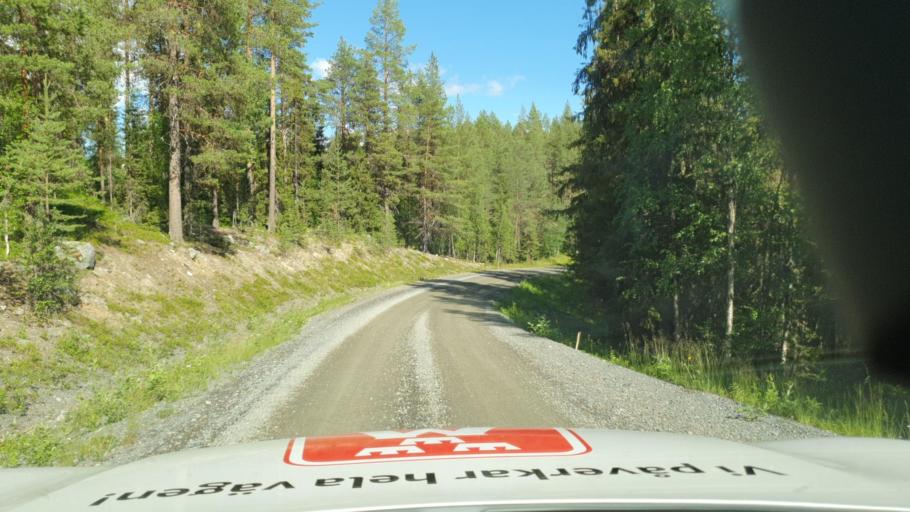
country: SE
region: Vaesterbotten
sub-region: Sorsele Kommun
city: Sorsele
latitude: 65.4116
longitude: 17.5520
